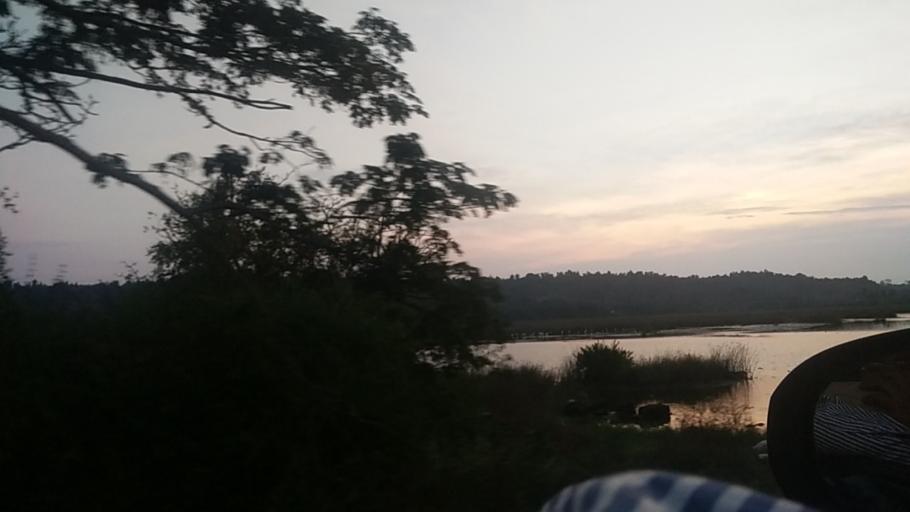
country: IN
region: Goa
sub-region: North Goa
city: Taleigao
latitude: 15.4711
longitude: 73.8377
